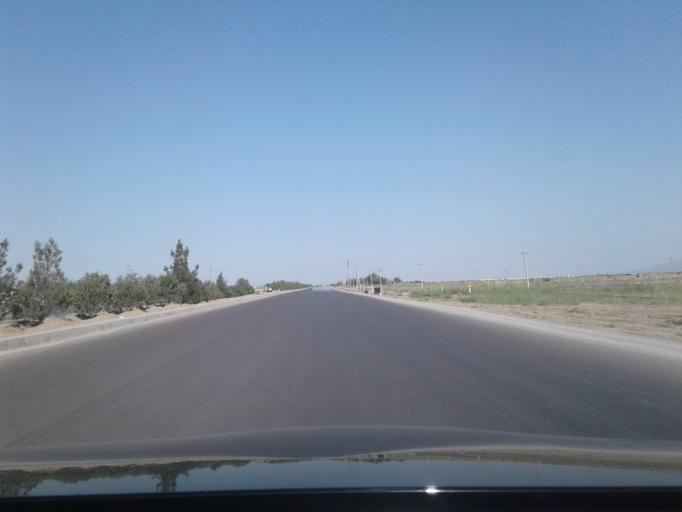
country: TM
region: Ahal
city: Abadan
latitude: 38.1735
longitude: 57.9031
